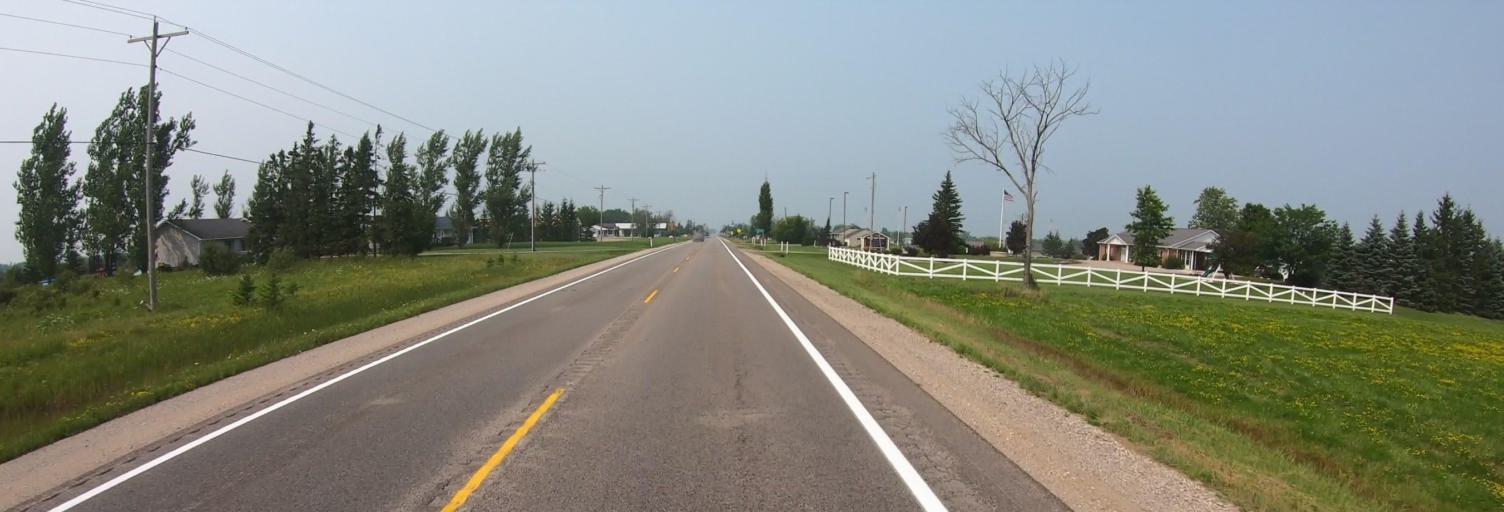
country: US
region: Michigan
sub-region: Chippewa County
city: Sault Ste. Marie
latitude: 46.1494
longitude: -84.3634
